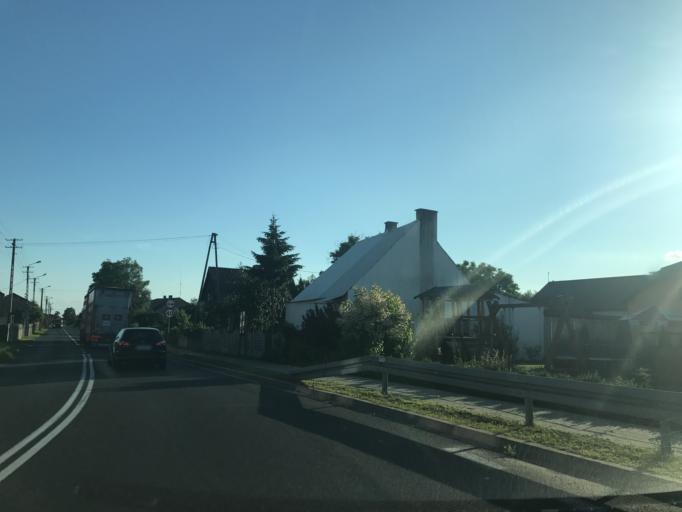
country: PL
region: Greater Poland Voivodeship
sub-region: Powiat koninski
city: Rychwal
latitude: 52.0597
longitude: 18.1308
